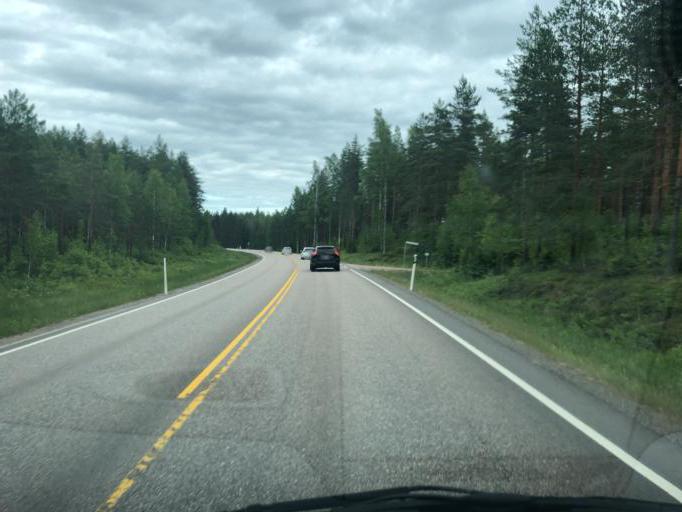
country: FI
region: Southern Savonia
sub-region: Mikkeli
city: Maentyharju
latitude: 61.1495
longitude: 27.1357
